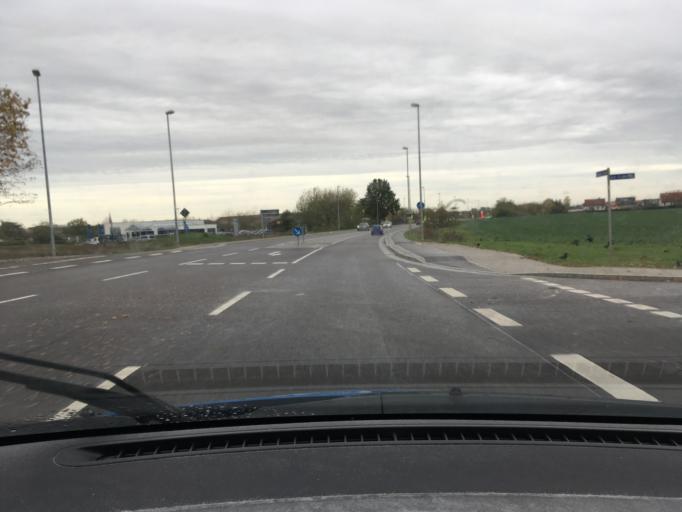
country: DE
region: Saxony-Anhalt
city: Zerbst
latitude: 51.9561
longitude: 12.1015
